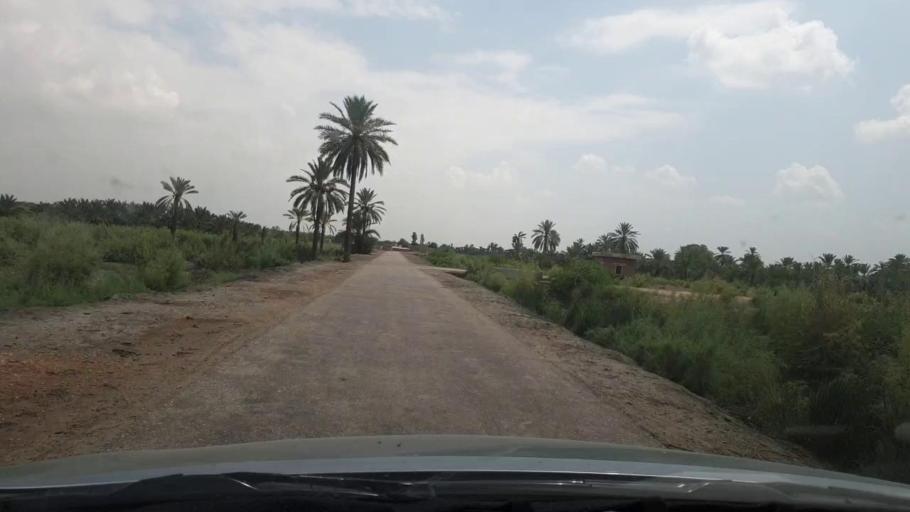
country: PK
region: Sindh
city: Kot Diji
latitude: 27.4037
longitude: 68.7388
